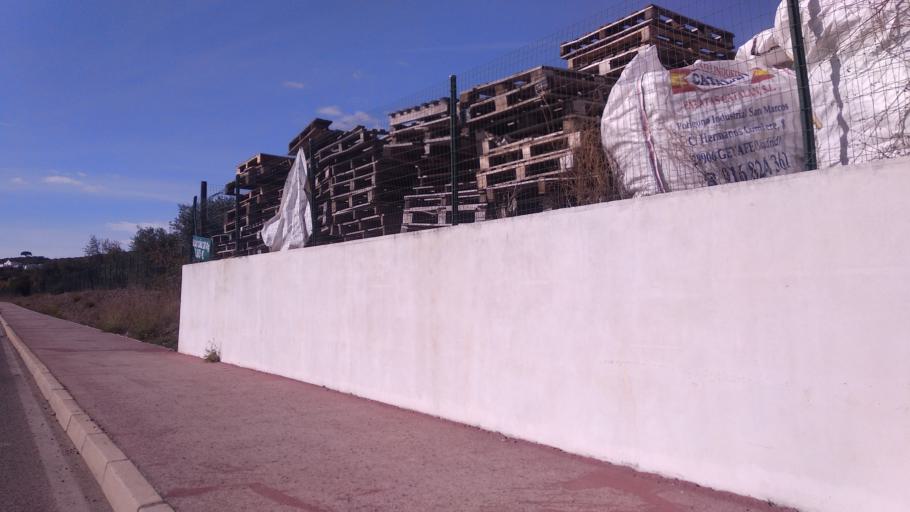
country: PT
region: Faro
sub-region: Sao Bras de Alportel
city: Sao Bras de Alportel
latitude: 37.1592
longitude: -7.8901
